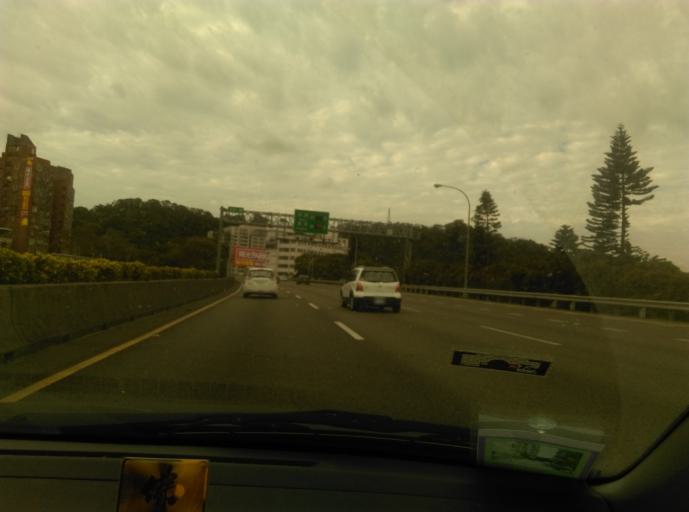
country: TW
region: Taipei
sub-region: Taipei
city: Banqiao
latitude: 24.9760
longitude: 121.5186
